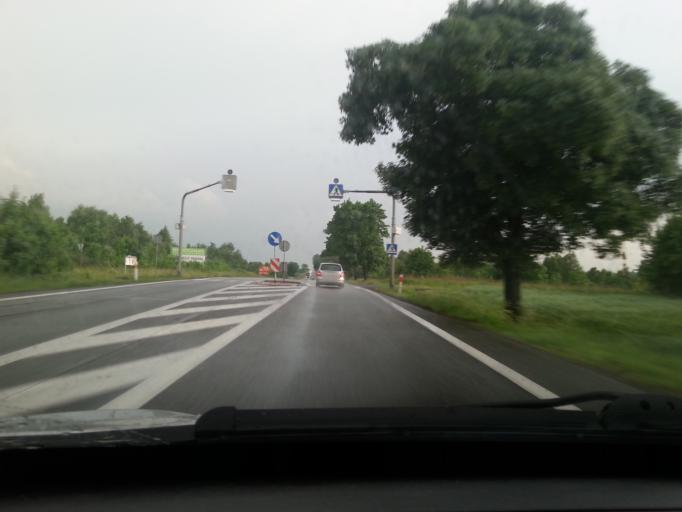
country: PL
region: Lodz Voivodeship
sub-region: Powiat zgierski
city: Strykow
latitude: 51.8572
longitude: 19.5647
